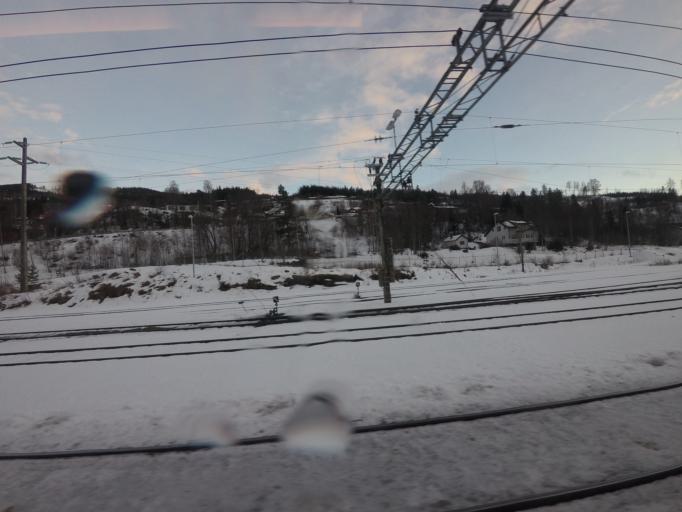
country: NO
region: Buskerud
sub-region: Al
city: Al
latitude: 60.6265
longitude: 8.5633
